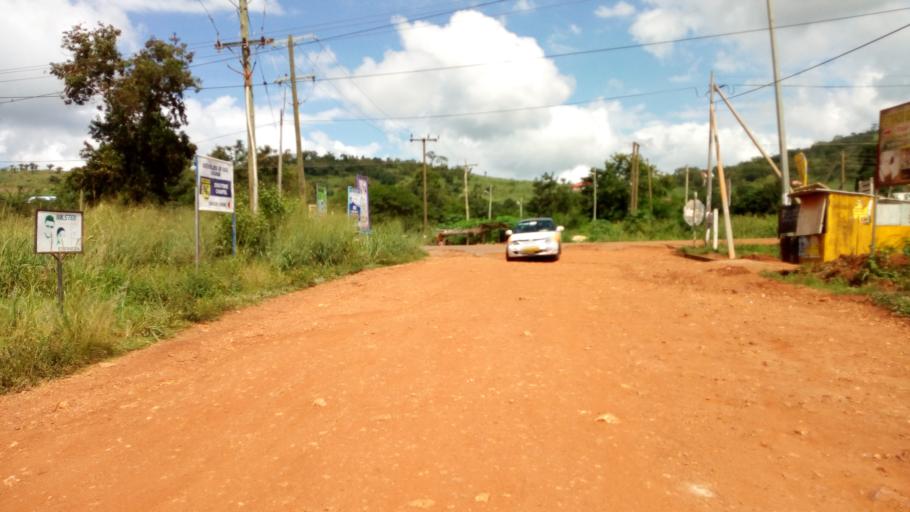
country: GH
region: Volta
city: Ho
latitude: 6.5940
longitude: 0.4399
